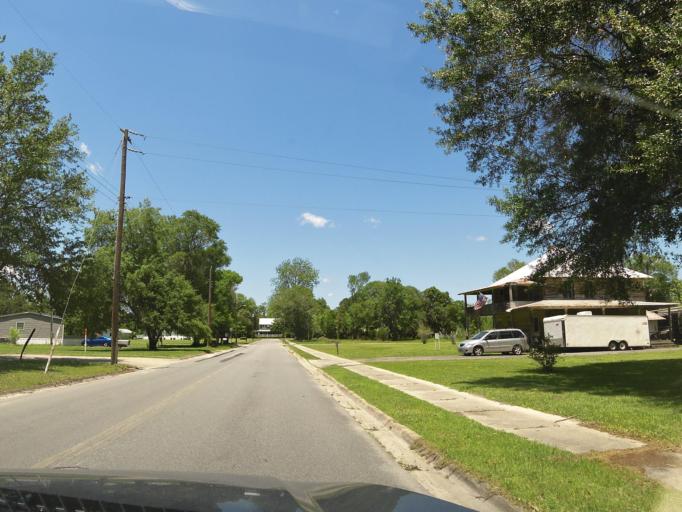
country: US
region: Florida
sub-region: Bradford County
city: Starke
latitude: 30.0449
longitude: -82.0738
